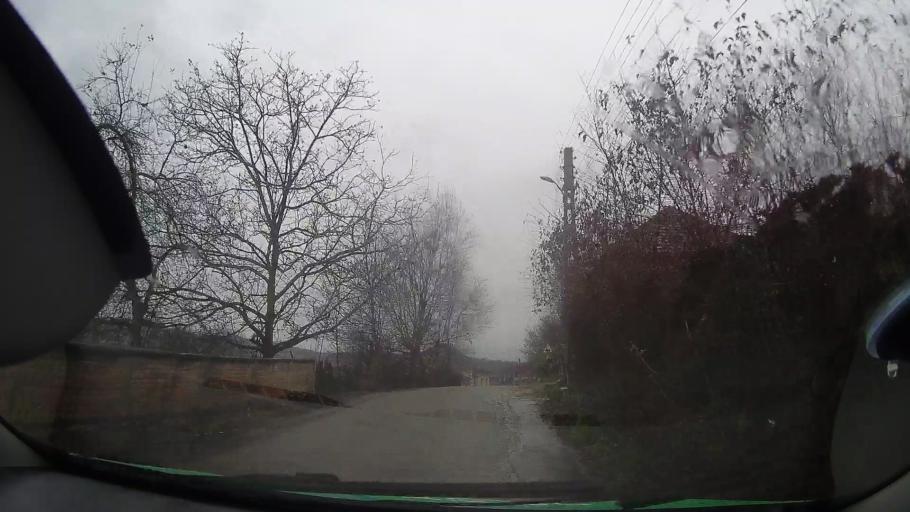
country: RO
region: Bihor
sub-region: Comuna Uileacu de Beius
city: Forau
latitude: 46.7122
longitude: 22.2285
